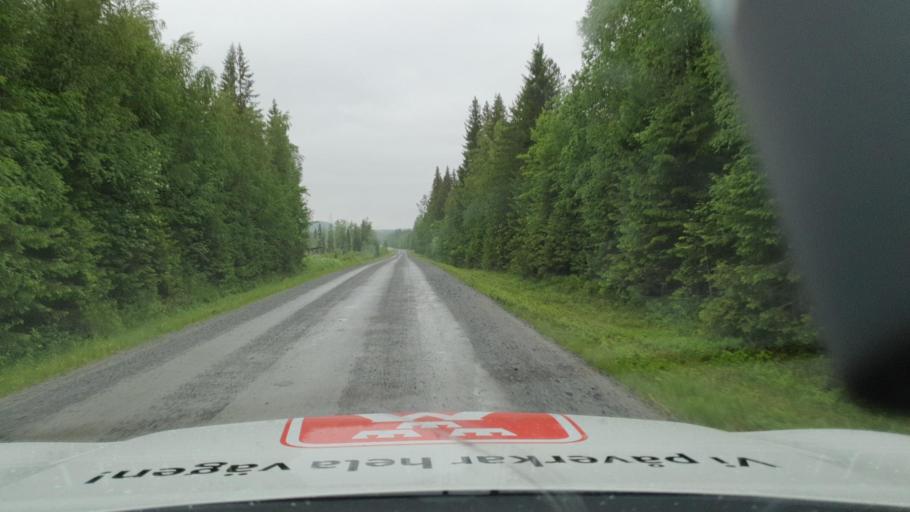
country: SE
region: Vaesterbotten
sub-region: Nordmalings Kommun
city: Nordmaling
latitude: 63.8329
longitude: 19.4868
